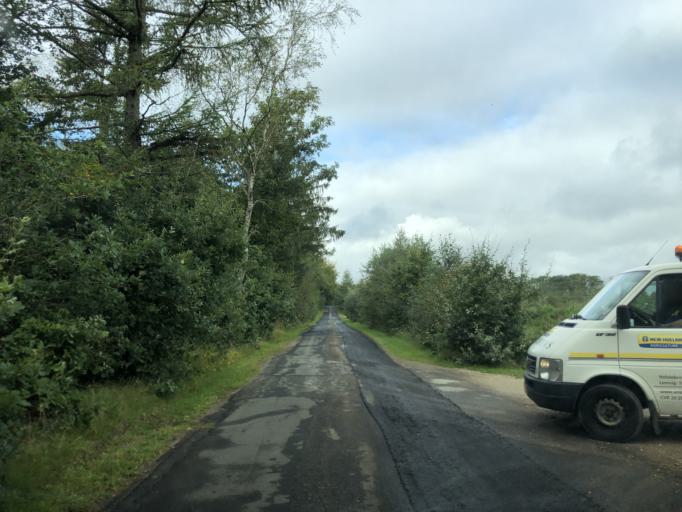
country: DK
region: Central Jutland
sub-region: Holstebro Kommune
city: Ulfborg
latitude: 56.3055
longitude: 8.4338
